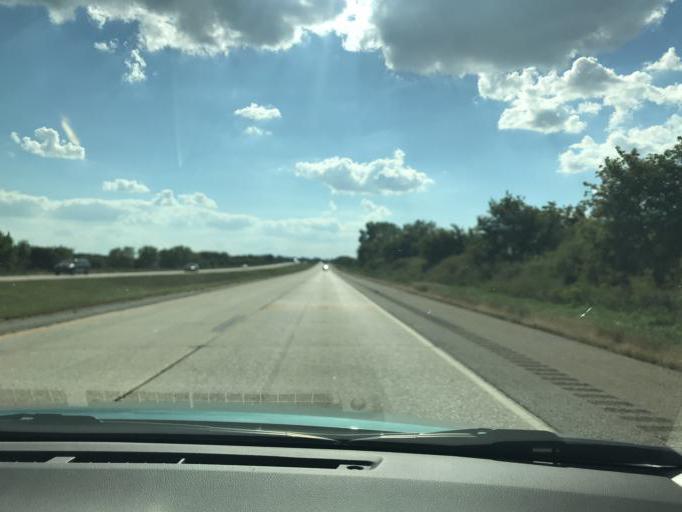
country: US
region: Wisconsin
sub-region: Walworth County
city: Darien
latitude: 42.5935
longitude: -88.7473
